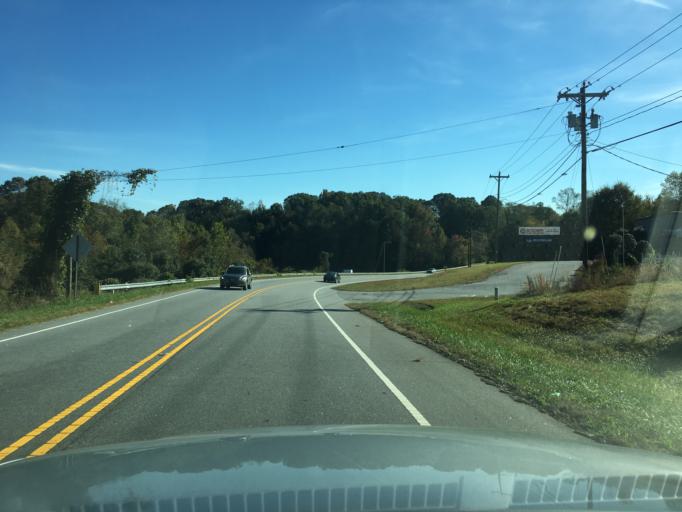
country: US
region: North Carolina
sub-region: Catawba County
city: Saint Stephens
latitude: 35.7100
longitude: -81.2785
